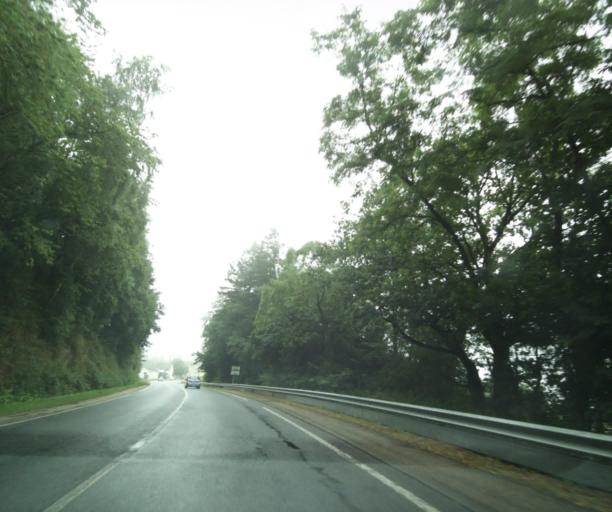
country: FR
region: Midi-Pyrenees
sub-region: Departement de l'Aveyron
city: Baraqueville
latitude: 44.2733
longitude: 2.4287
